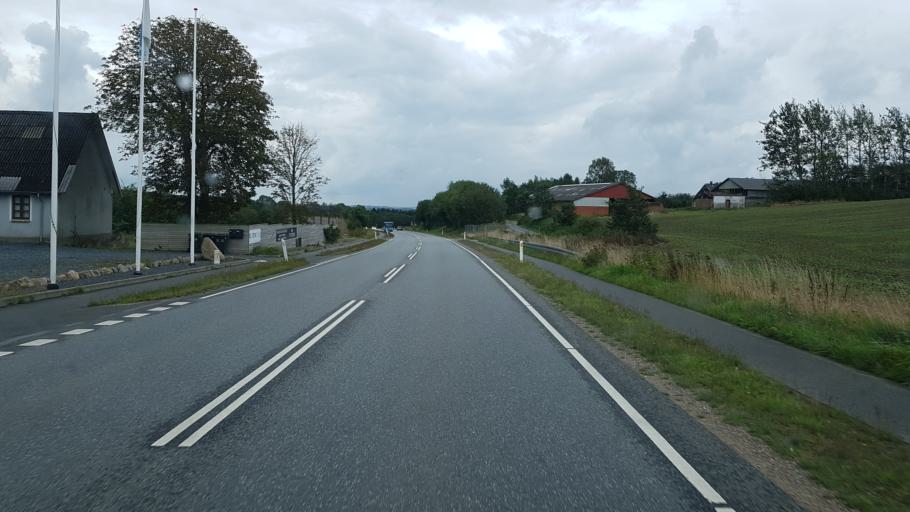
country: DK
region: Central Jutland
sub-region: Horsens Kommune
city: Braedstrup
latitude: 55.9095
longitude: 9.7204
